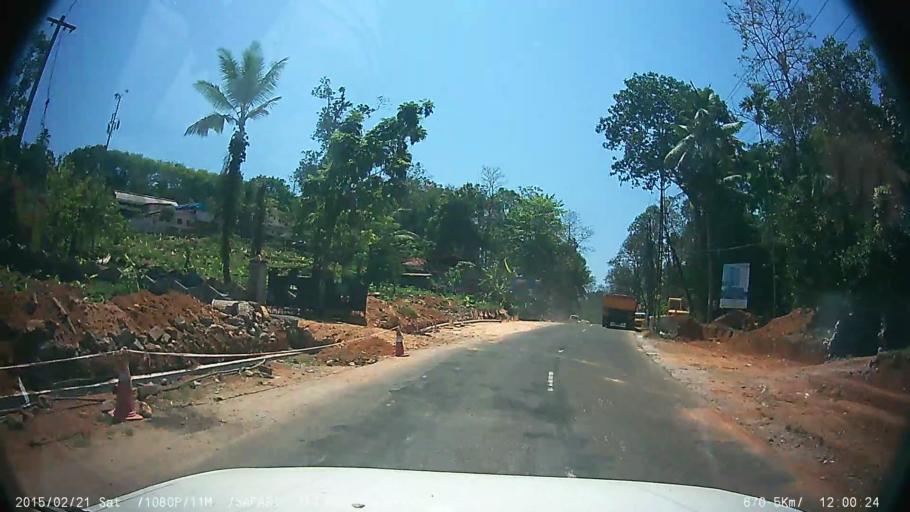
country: IN
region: Kerala
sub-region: Kottayam
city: Lalam
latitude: 9.7292
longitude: 76.6932
